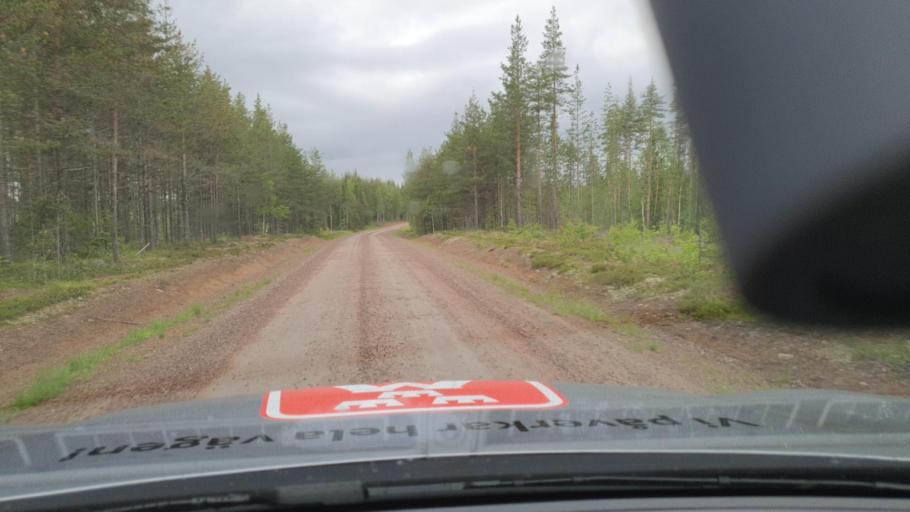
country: SE
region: Norrbotten
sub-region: Overkalix Kommun
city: OEverkalix
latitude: 66.6215
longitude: 22.7265
